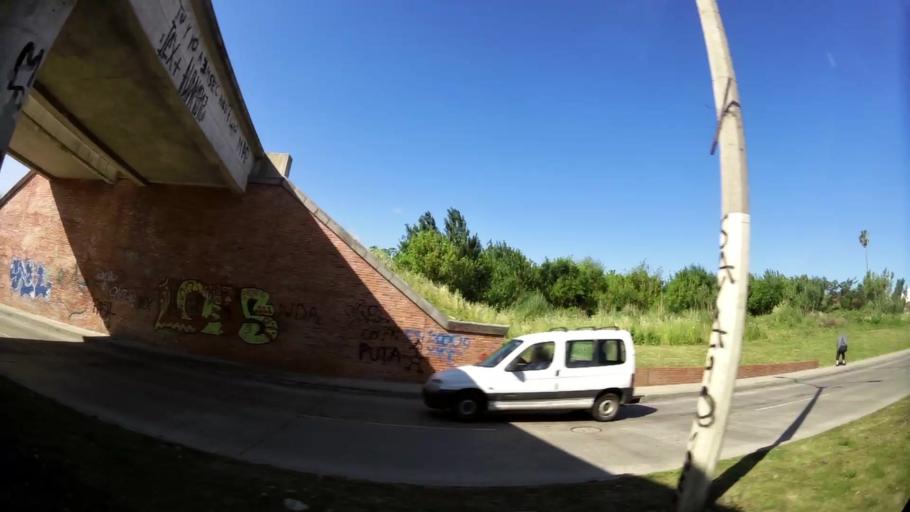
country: UY
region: Canelones
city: La Paz
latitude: -34.8290
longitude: -56.2177
